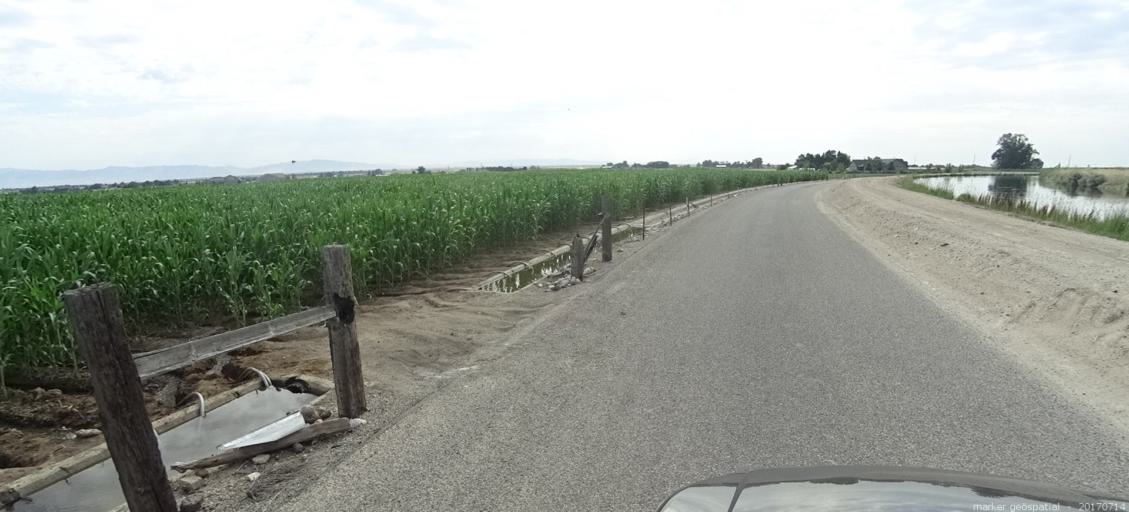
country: US
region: Idaho
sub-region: Ada County
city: Kuna
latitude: 43.4621
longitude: -116.3712
